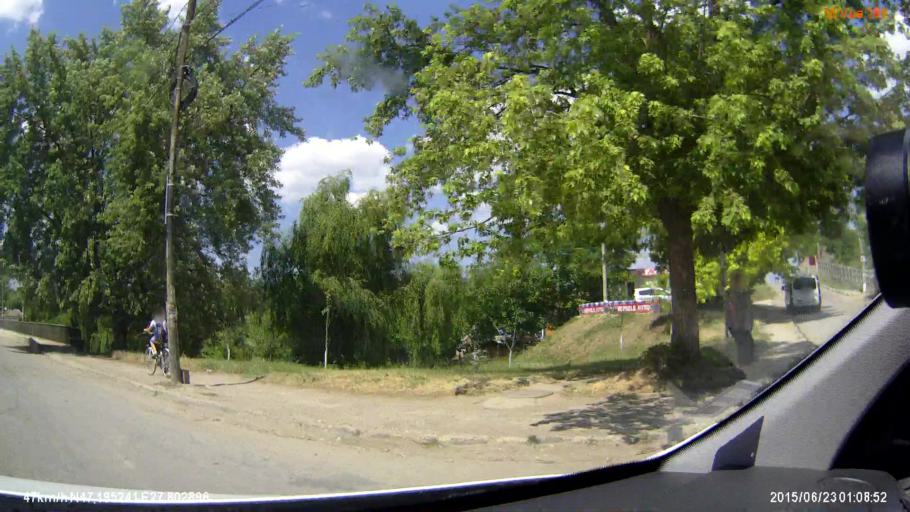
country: MD
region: Ungheni
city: Ungheni
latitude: 47.1951
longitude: 27.8030
